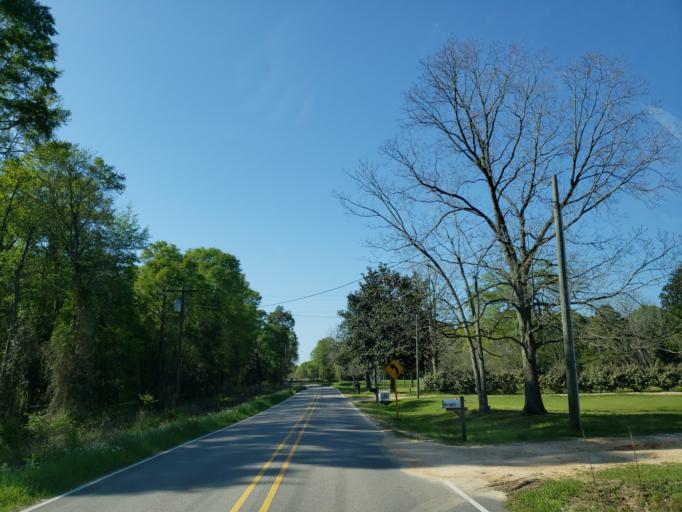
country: US
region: Mississippi
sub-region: Jones County
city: Ellisville
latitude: 31.5778
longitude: -89.3734
